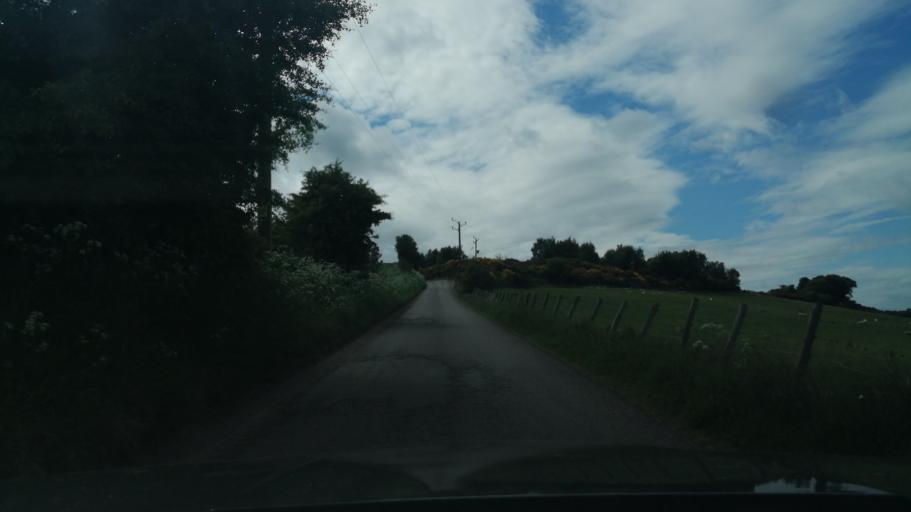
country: GB
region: Scotland
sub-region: Moray
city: Elgin
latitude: 57.6538
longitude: -3.2774
